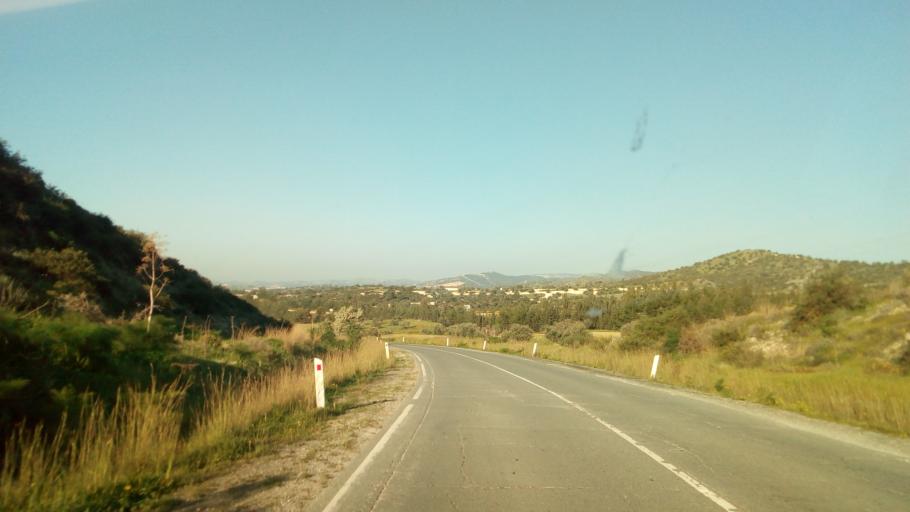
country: CY
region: Larnaka
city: Kofinou
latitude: 34.8491
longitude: 33.4446
